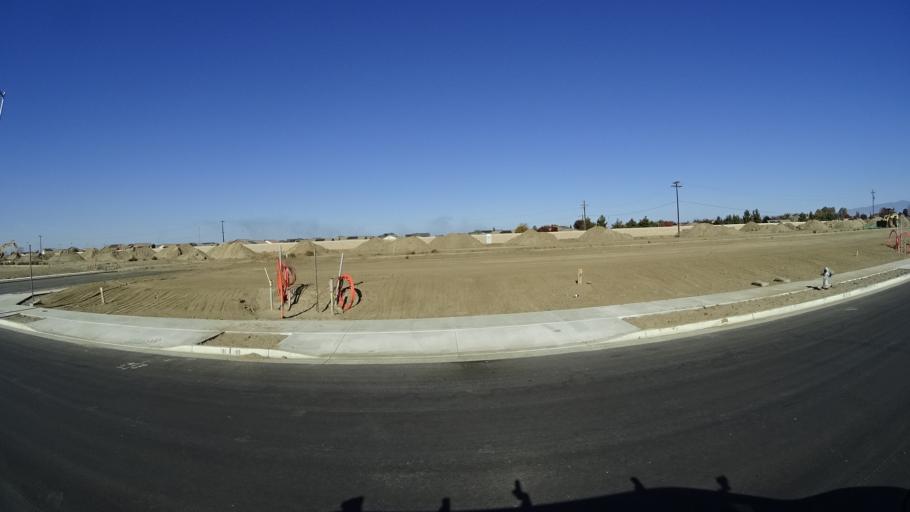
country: US
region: California
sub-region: Kern County
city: Greenfield
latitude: 35.2658
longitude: -119.0683
